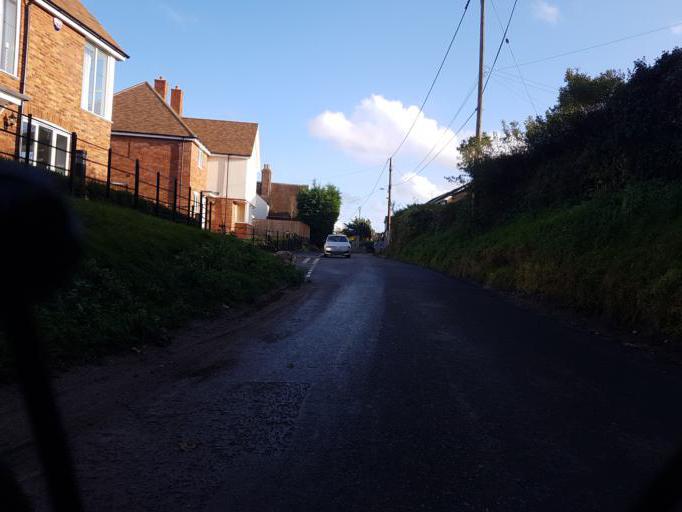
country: GB
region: England
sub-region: Kent
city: Newington
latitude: 51.3570
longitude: 0.6690
